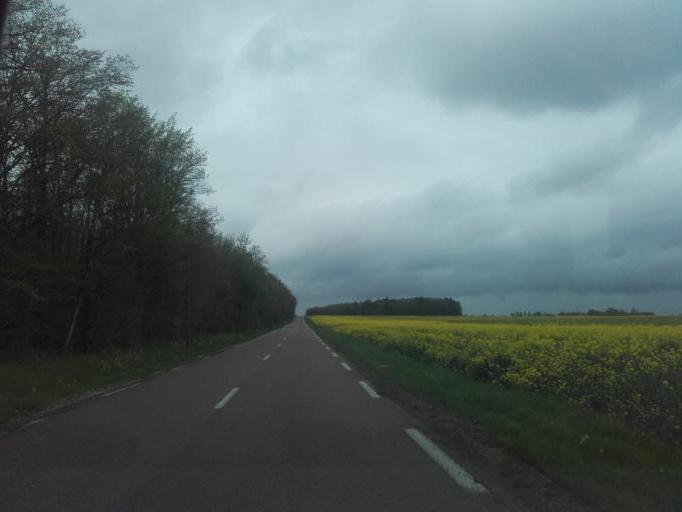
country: FR
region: Bourgogne
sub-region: Departement de l'Yonne
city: Joux-la-Ville
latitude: 47.6987
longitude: 3.8607
